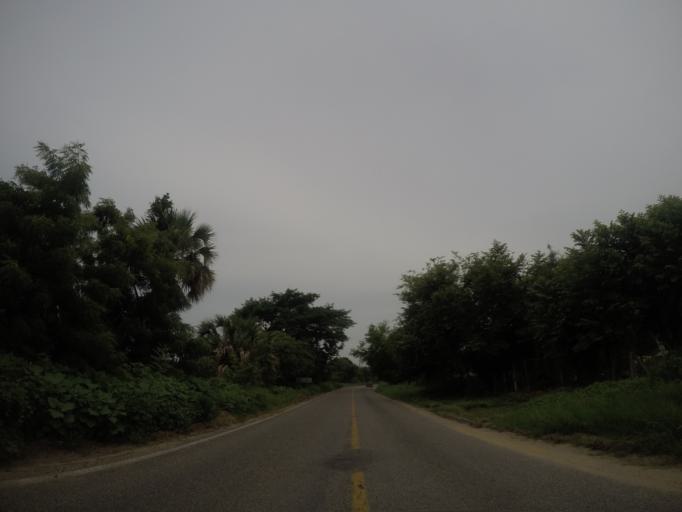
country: MX
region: Oaxaca
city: San Pedro Mixtepec
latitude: 15.9479
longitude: -97.1887
